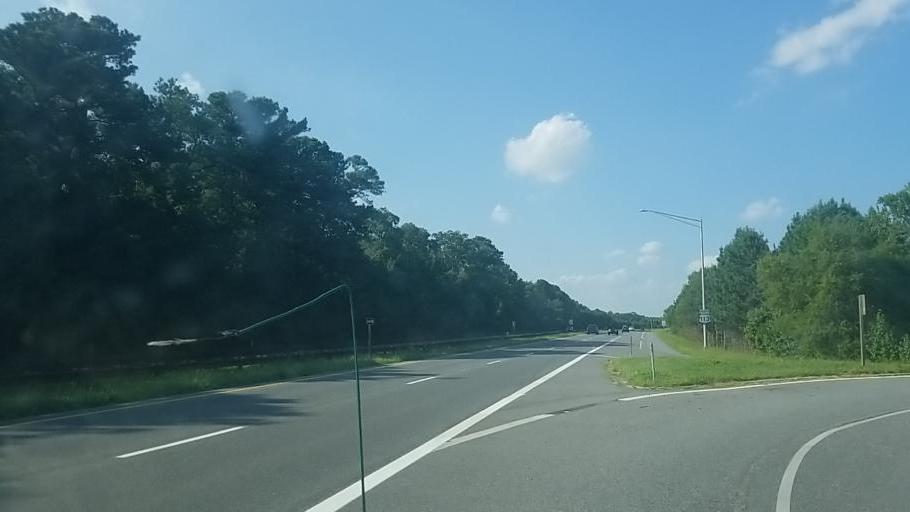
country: US
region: Maryland
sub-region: Worcester County
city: Berlin
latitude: 38.3578
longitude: -75.2136
